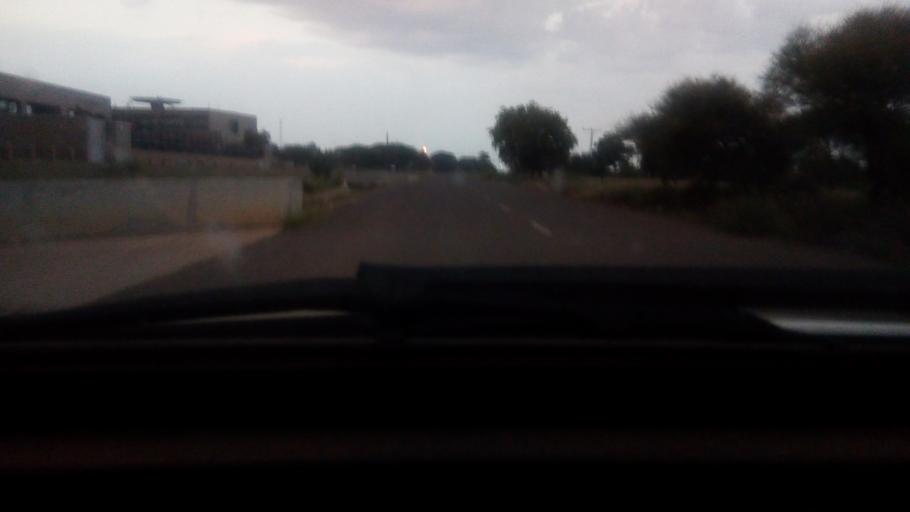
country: BW
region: Kweneng
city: Mmopone
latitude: -24.5894
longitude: 25.9170
